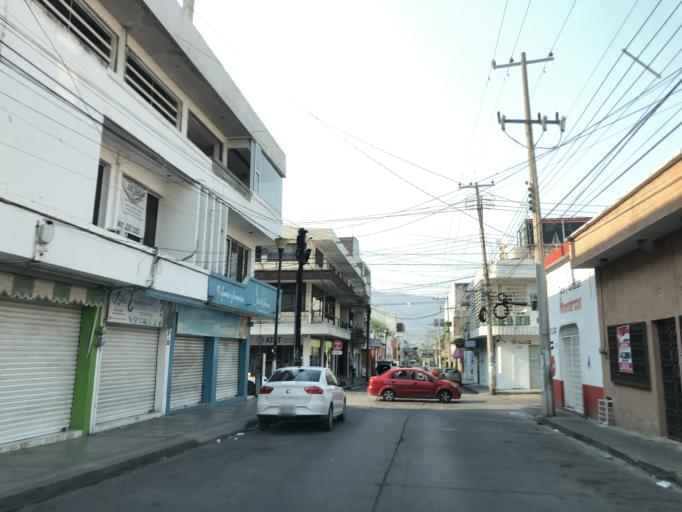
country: MX
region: Chiapas
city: Tuxtla Gutierrez
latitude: 16.7531
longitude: -93.1215
